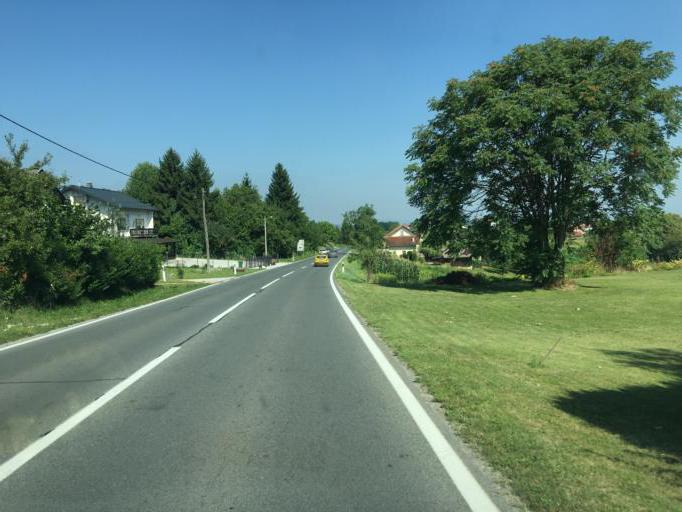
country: HR
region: Karlovacka
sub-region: Grad Karlovac
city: Karlovac
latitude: 45.4462
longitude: 15.5819
